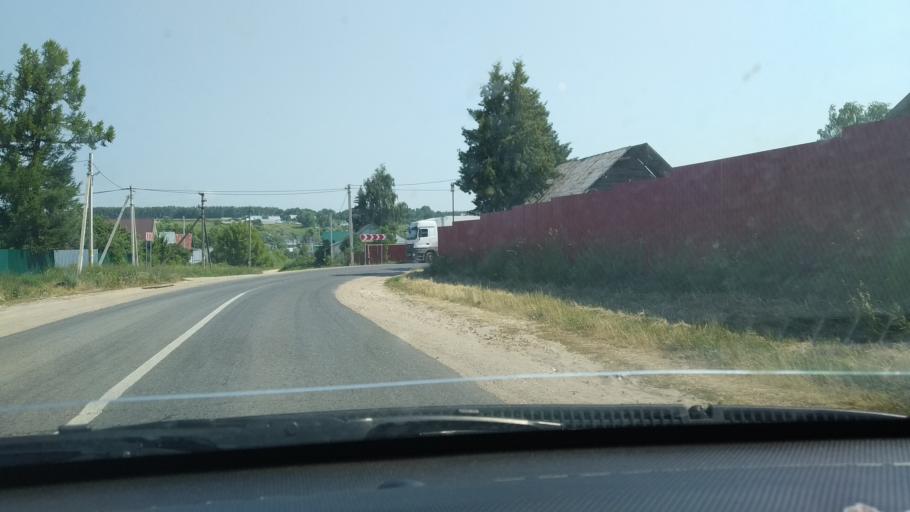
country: RU
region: Tatarstan
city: Osinovo
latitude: 55.9828
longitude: 48.7936
